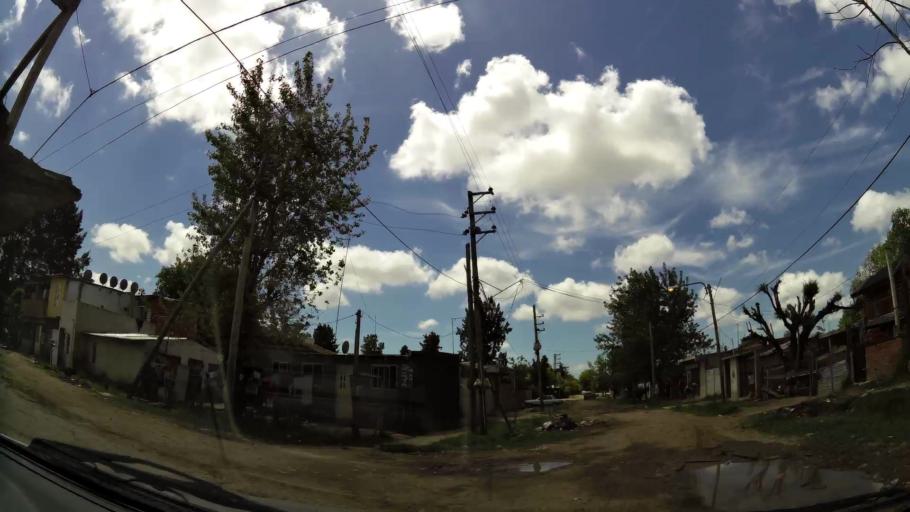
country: AR
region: Buenos Aires
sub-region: Partido de Quilmes
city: Quilmes
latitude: -34.8129
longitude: -58.2345
